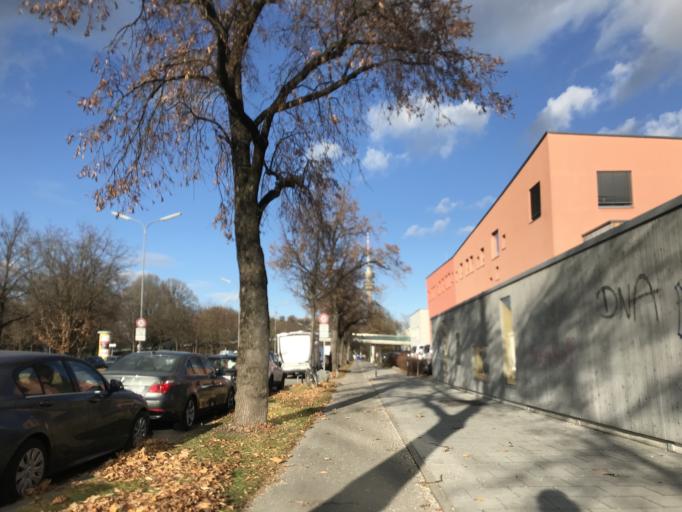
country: DE
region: Bavaria
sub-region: Upper Bavaria
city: Munich
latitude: 48.1626
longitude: 11.5532
